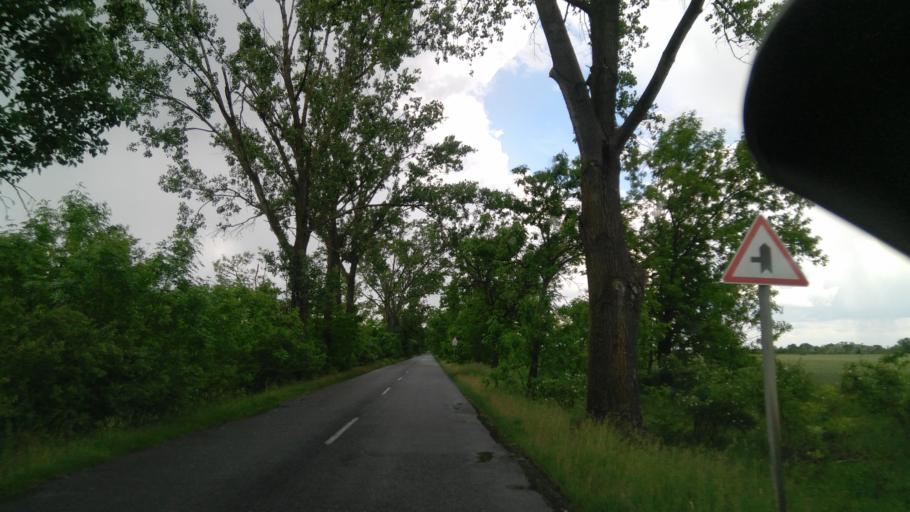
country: HU
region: Bekes
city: Fuzesgyarmat
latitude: 47.1355
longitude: 21.1582
